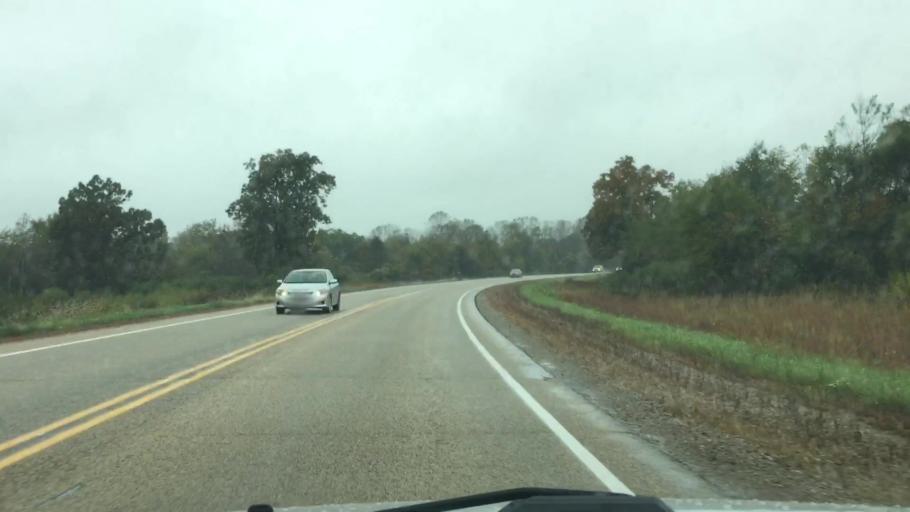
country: US
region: Wisconsin
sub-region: Jefferson County
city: Palmyra
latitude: 42.8801
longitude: -88.5499
